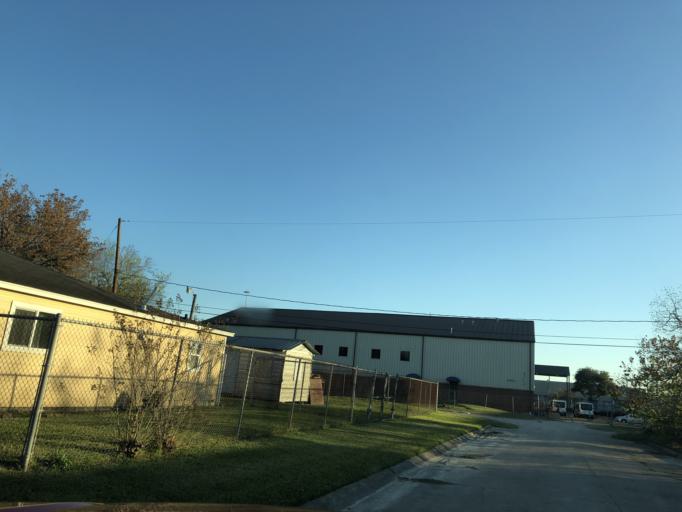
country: US
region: Texas
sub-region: Harris County
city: Jacinto City
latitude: 29.7603
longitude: -95.2666
